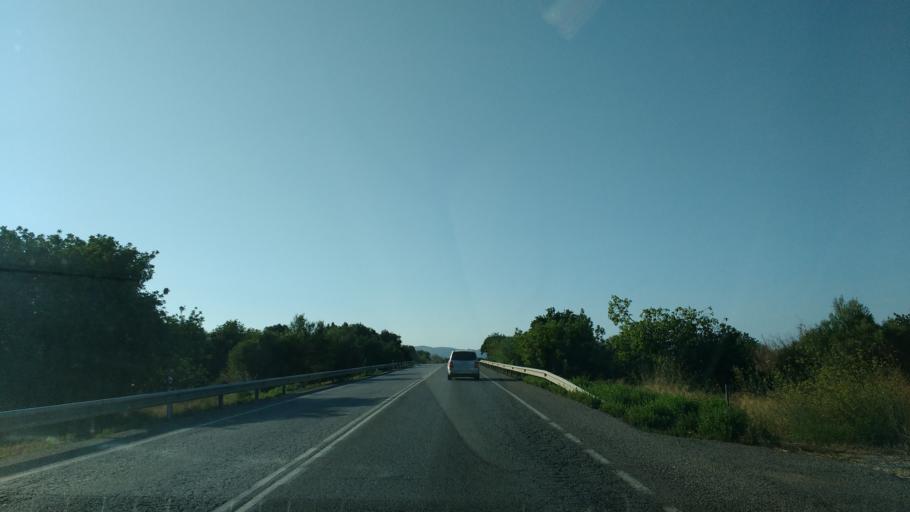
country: ES
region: Balearic Islands
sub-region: Illes Balears
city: Alcudia
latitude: 39.8383
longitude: 3.1008
